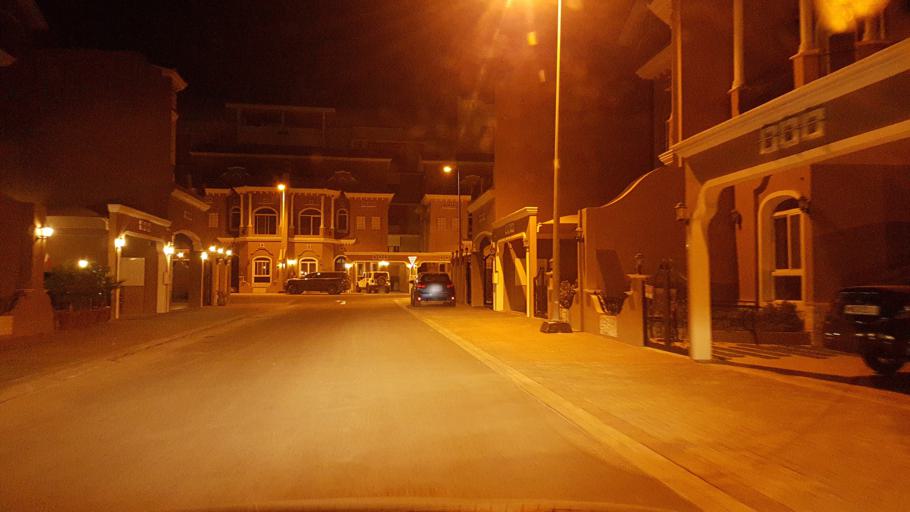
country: BH
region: Northern
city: Madinat `Isa
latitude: 26.1791
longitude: 50.4799
